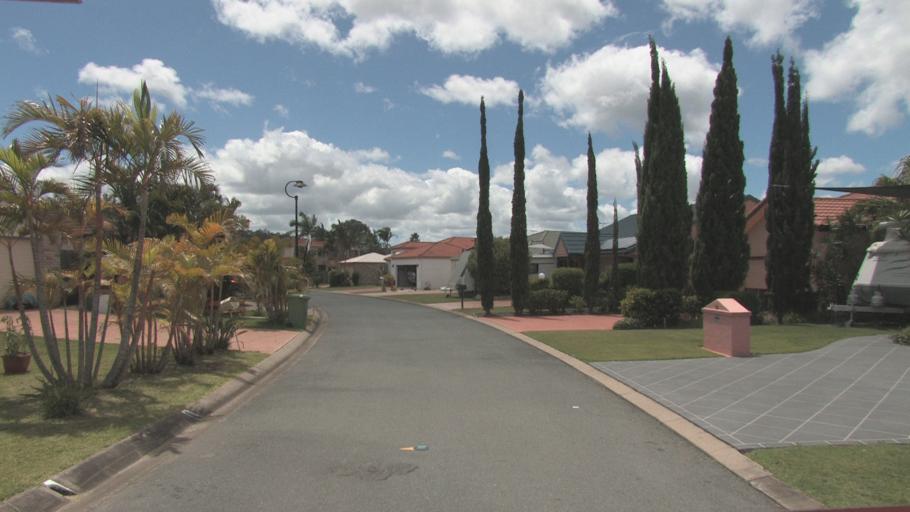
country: AU
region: Queensland
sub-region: Logan
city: Beenleigh
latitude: -27.6759
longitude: 153.2125
